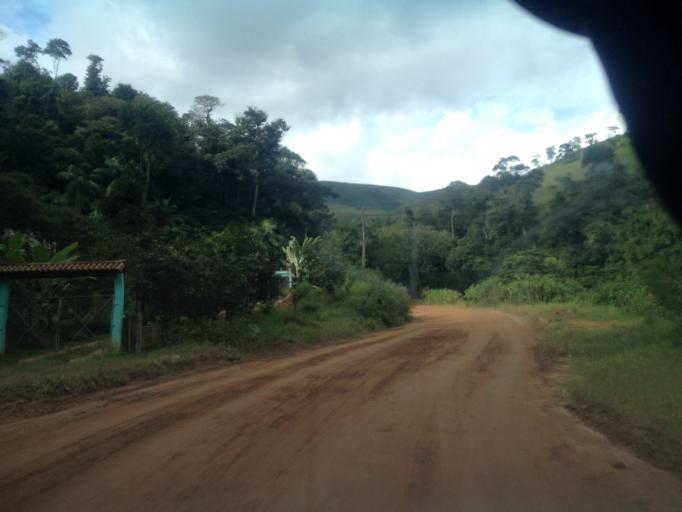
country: BR
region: Rio de Janeiro
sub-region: Quatis
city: Quatis
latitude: -22.2322
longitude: -44.2585
